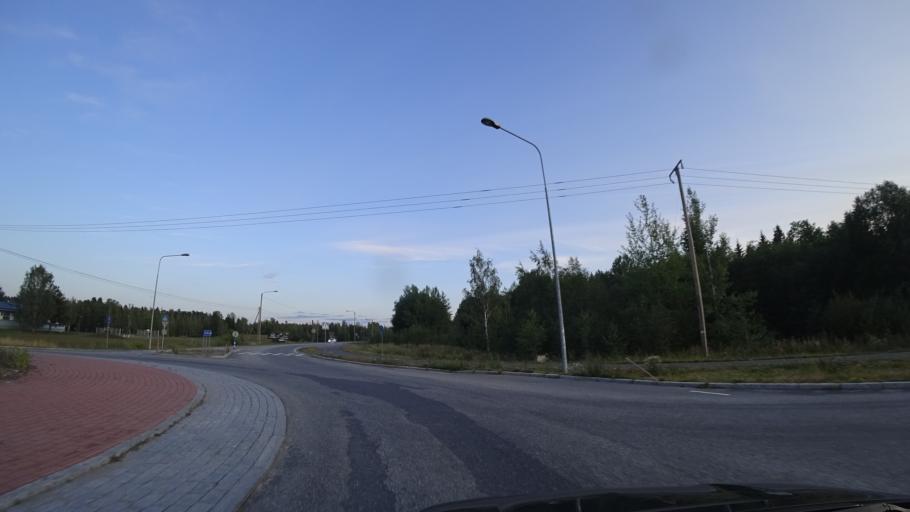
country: FI
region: Haeme
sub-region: Riihimaeki
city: Riihimaeki
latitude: 60.7370
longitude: 24.7324
